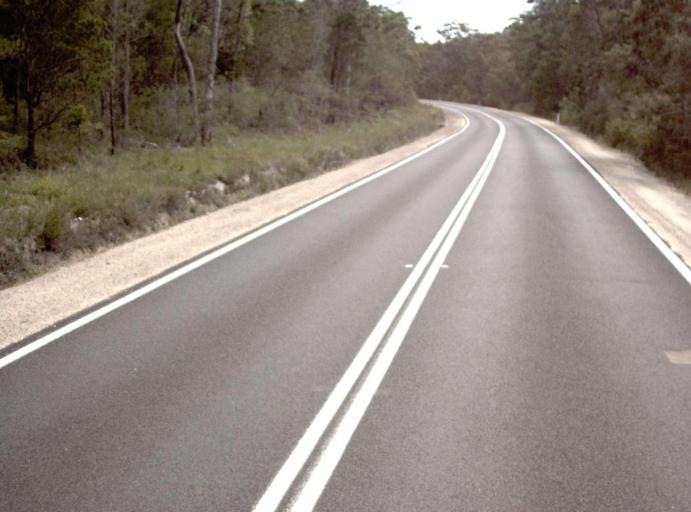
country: AU
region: New South Wales
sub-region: Bega Valley
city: Eden
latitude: -37.4490
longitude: 149.6229
